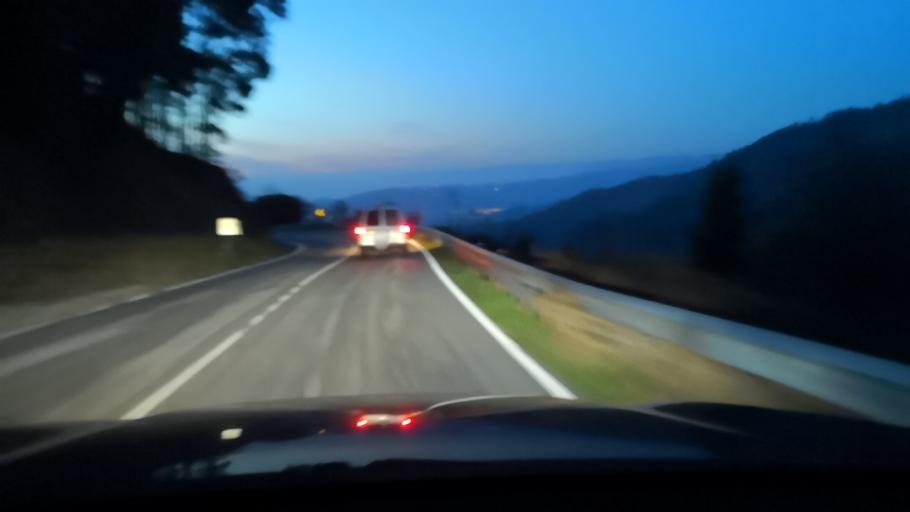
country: PT
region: Porto
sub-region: Baiao
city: Baiao
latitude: 41.2271
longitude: -8.0030
